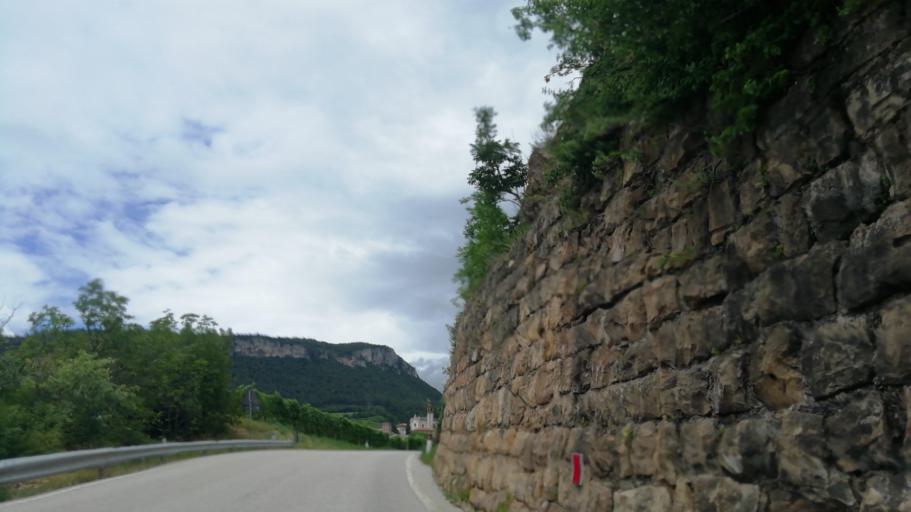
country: IT
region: Trentino-Alto Adige
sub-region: Provincia di Trento
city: Verla
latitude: 46.1614
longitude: 11.1585
